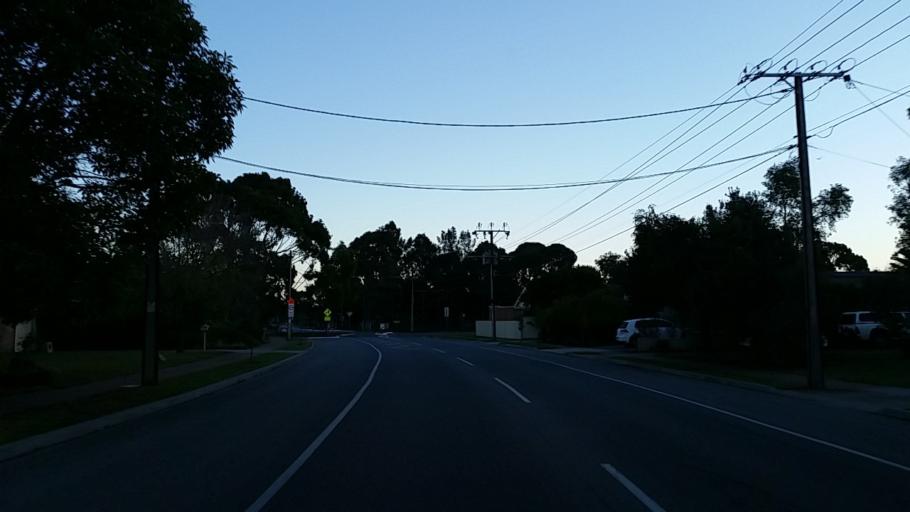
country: AU
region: South Australia
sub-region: Charles Sturt
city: Henley Beach
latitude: -34.9214
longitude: 138.5048
